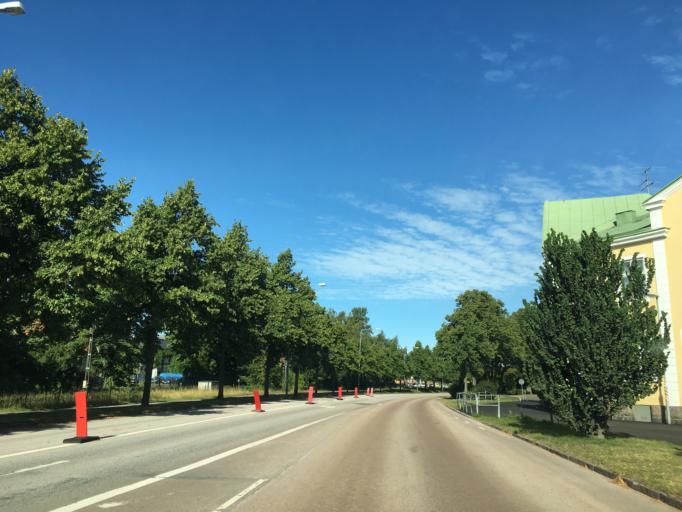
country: SE
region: Kalmar
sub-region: Kalmar Kommun
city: Kalmar
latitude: 56.6640
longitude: 16.3474
